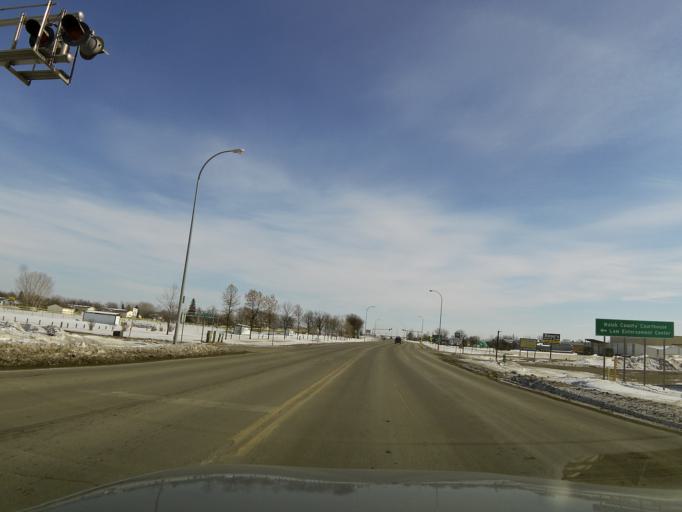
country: US
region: North Dakota
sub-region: Walsh County
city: Grafton
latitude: 48.4124
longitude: -97.4062
